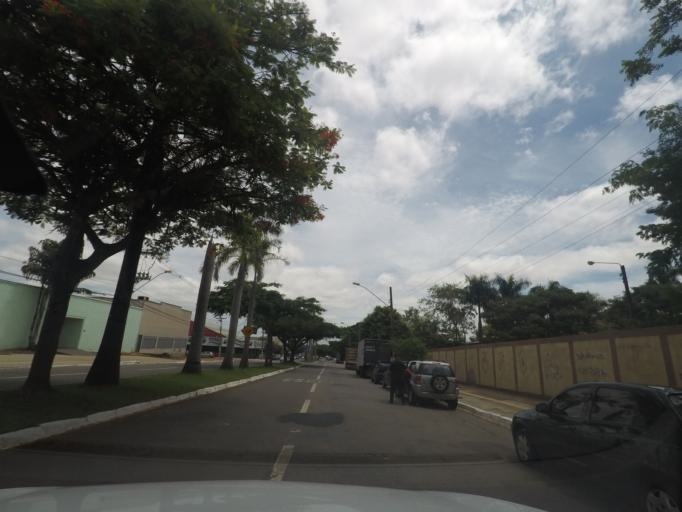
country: BR
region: Goias
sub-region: Goiania
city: Goiania
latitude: -16.6704
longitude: -49.2436
